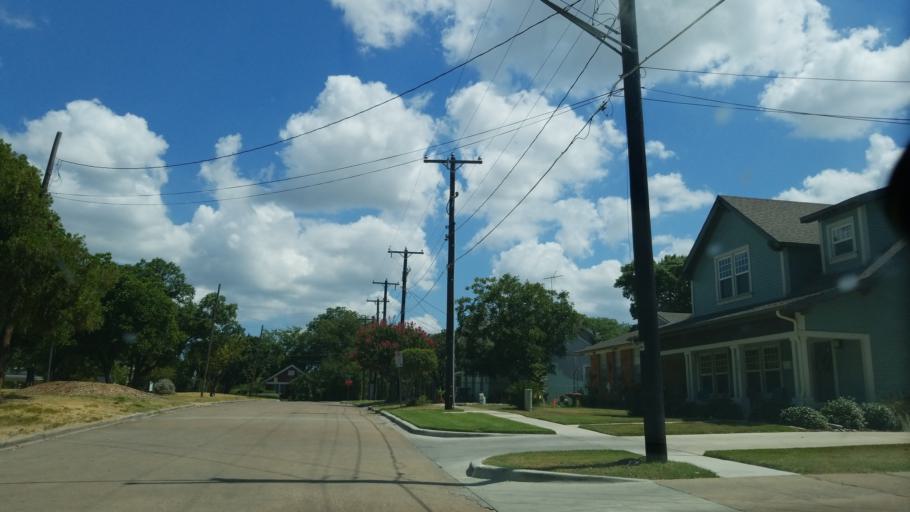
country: US
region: Texas
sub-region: Dallas County
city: Dallas
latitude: 32.7544
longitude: -96.8327
